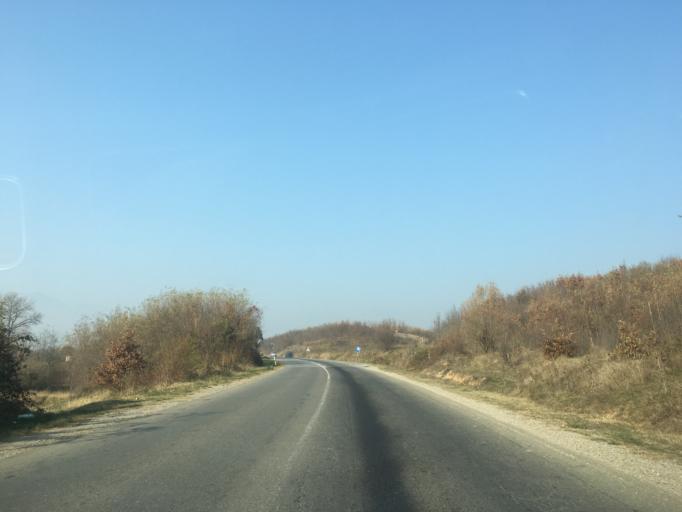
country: XK
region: Pec
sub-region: Komuna e Pejes
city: Kosuriq
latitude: 42.6398
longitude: 20.4266
